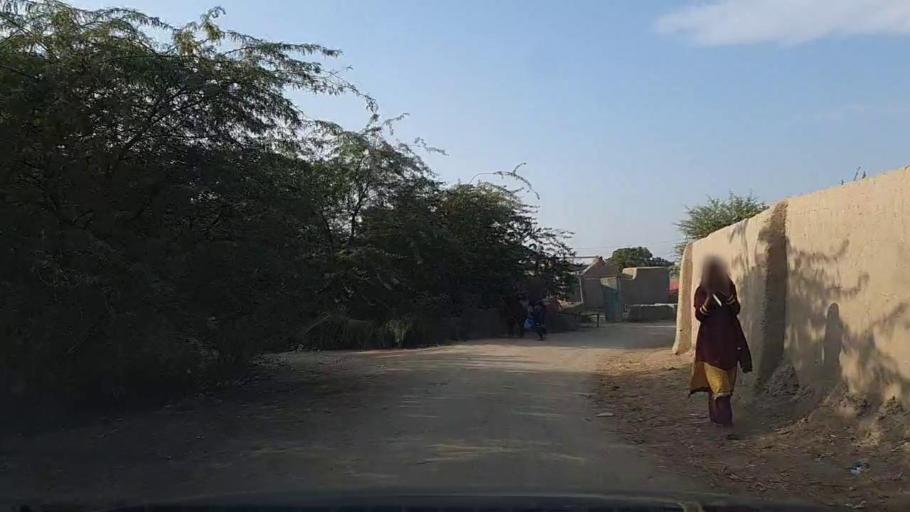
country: PK
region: Sindh
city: Daur
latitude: 26.4144
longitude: 68.4334
